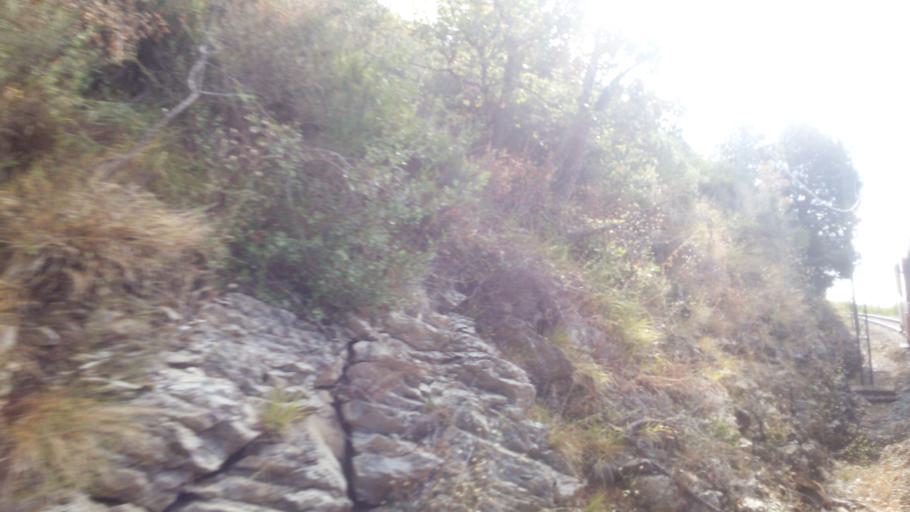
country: IT
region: Liguria
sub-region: Provincia di Genova
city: Genoa
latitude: 44.4398
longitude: 8.9407
